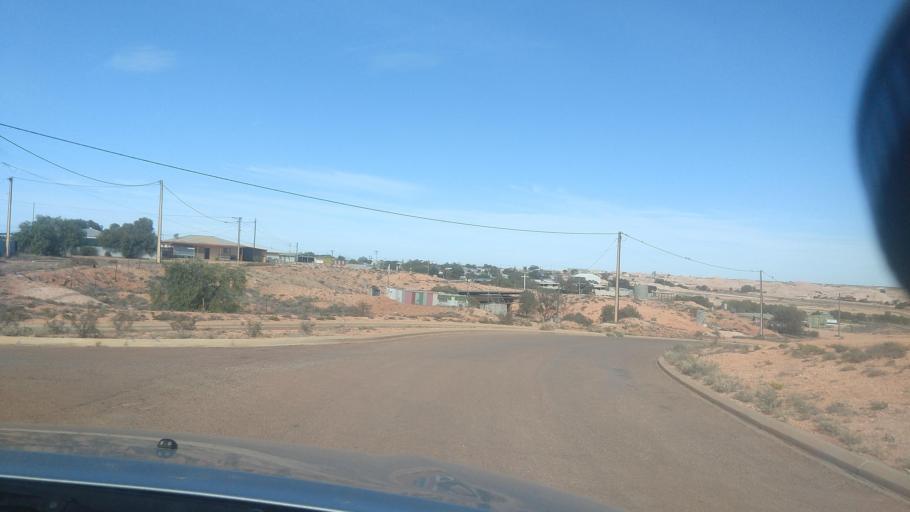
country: AU
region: South Australia
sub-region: Coober Pedy
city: Coober Pedy
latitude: -29.0134
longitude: 134.7495
